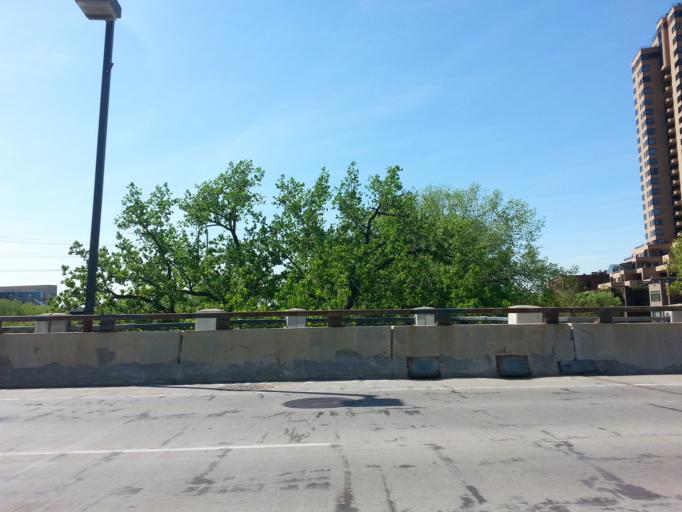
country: US
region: Minnesota
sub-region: Hennepin County
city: Minneapolis
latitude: 44.9844
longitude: -93.2568
